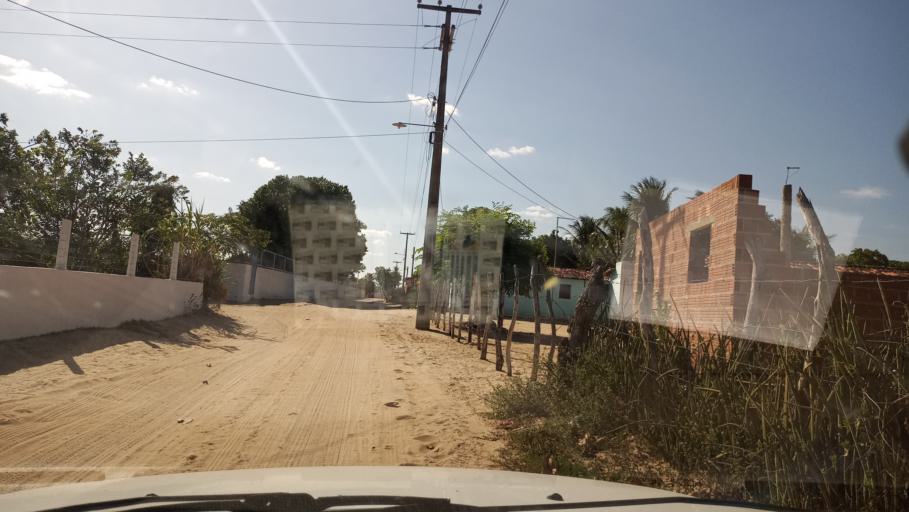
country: BR
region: Rio Grande do Norte
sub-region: Brejinho
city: Brejinho
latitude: -6.1750
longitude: -35.4649
